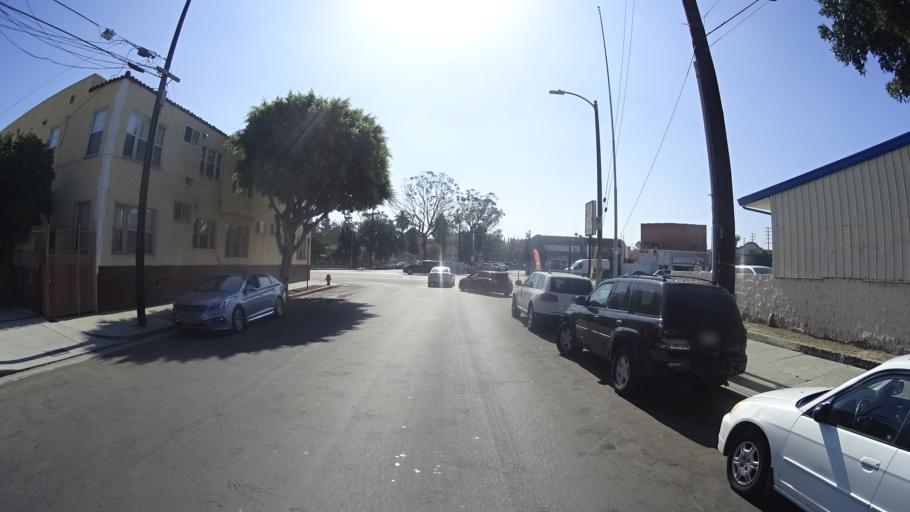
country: US
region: California
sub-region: Los Angeles County
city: Los Angeles
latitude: 34.0359
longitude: -118.2846
